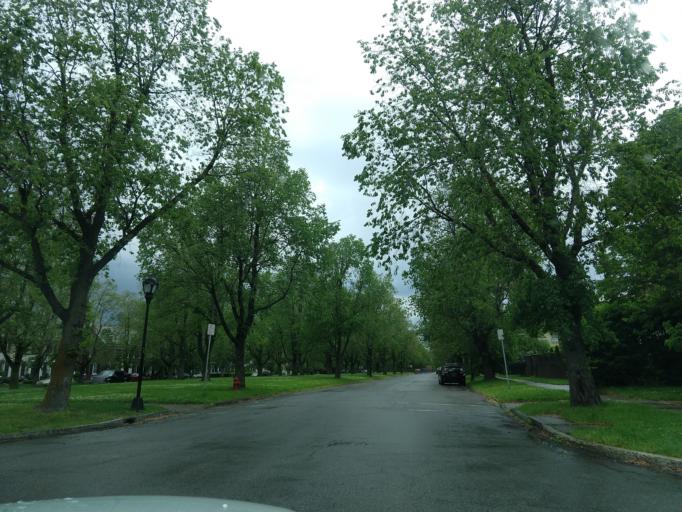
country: US
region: New York
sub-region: Erie County
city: Buffalo
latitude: 42.9210
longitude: -78.8679
